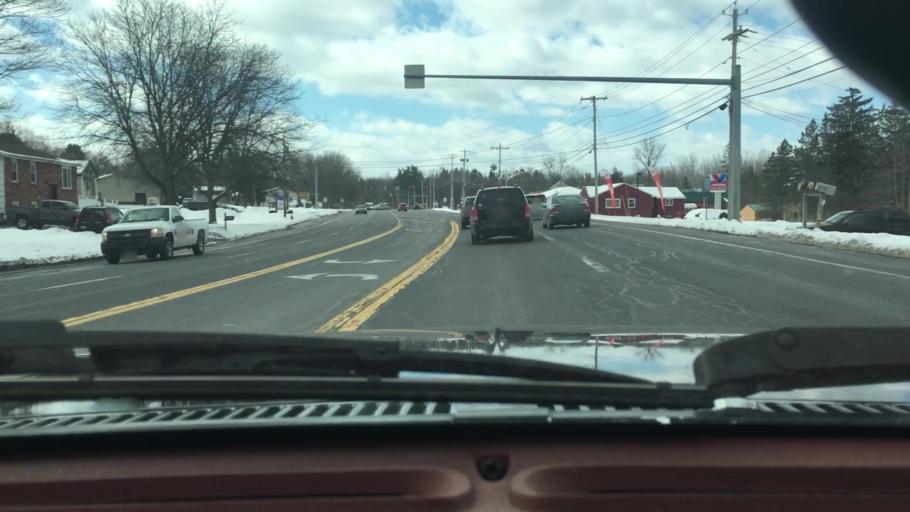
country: US
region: New York
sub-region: Onondaga County
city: Liverpool
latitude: 43.1518
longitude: -76.2291
